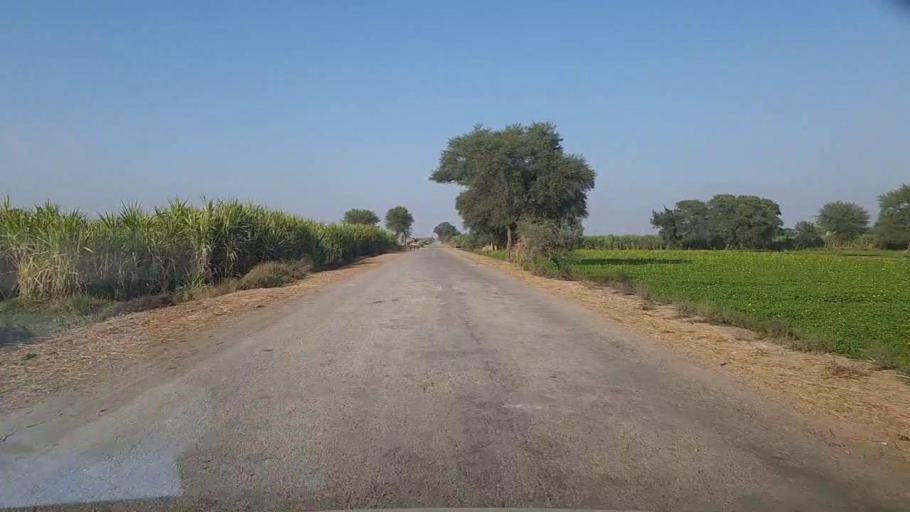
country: PK
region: Sindh
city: Phulji
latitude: 26.8515
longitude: 67.7937
